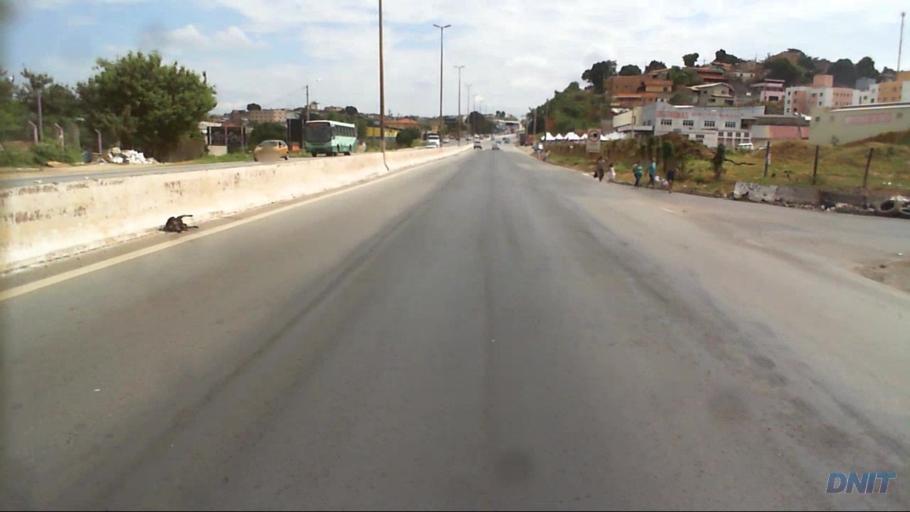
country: BR
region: Minas Gerais
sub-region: Belo Horizonte
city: Belo Horizonte
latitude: -19.8571
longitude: -43.9018
